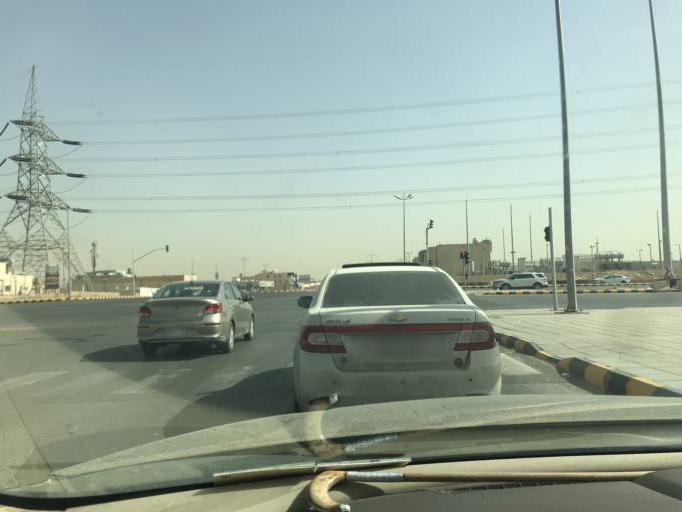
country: SA
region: Ar Riyad
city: Riyadh
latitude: 24.8170
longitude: 46.7316
